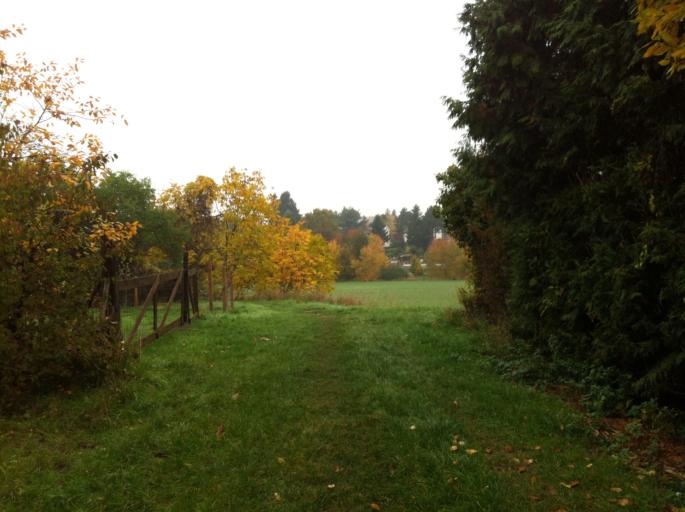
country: DE
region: Rheinland-Pfalz
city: Budenheim
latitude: 49.9958
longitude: 8.1955
